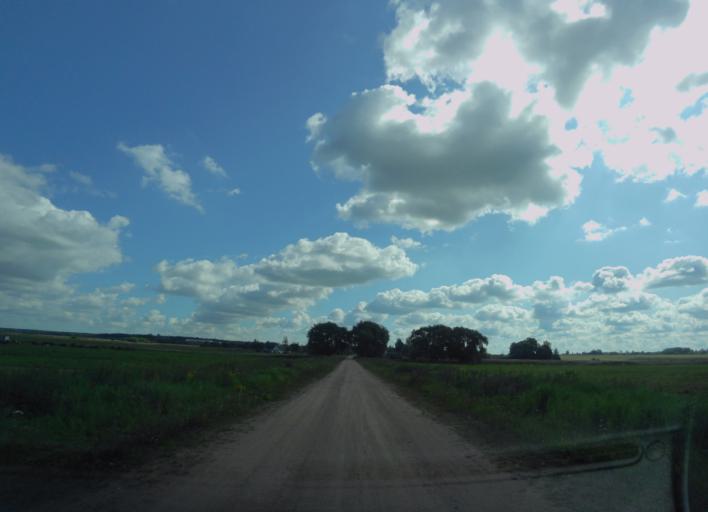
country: BY
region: Minsk
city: Zyembin
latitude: 54.3780
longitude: 28.3617
